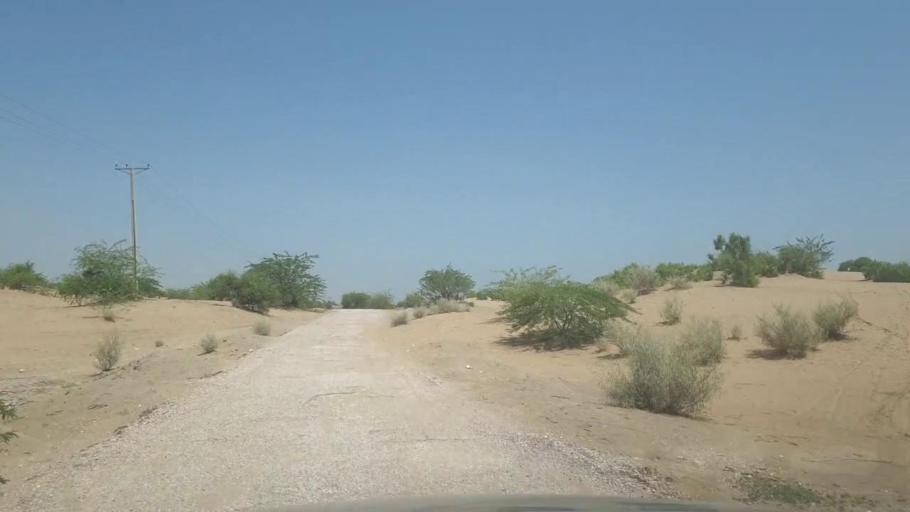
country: PK
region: Sindh
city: Kot Diji
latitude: 27.3272
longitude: 69.0120
